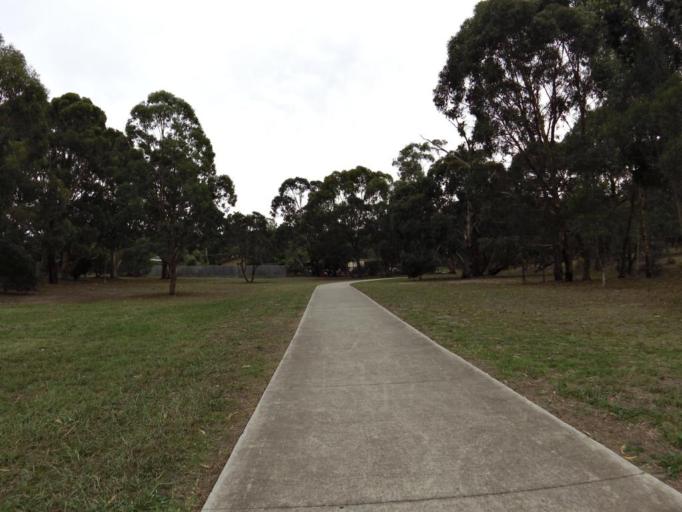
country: AU
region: Victoria
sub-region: Hume
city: Sunbury
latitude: -37.5674
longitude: 144.7235
